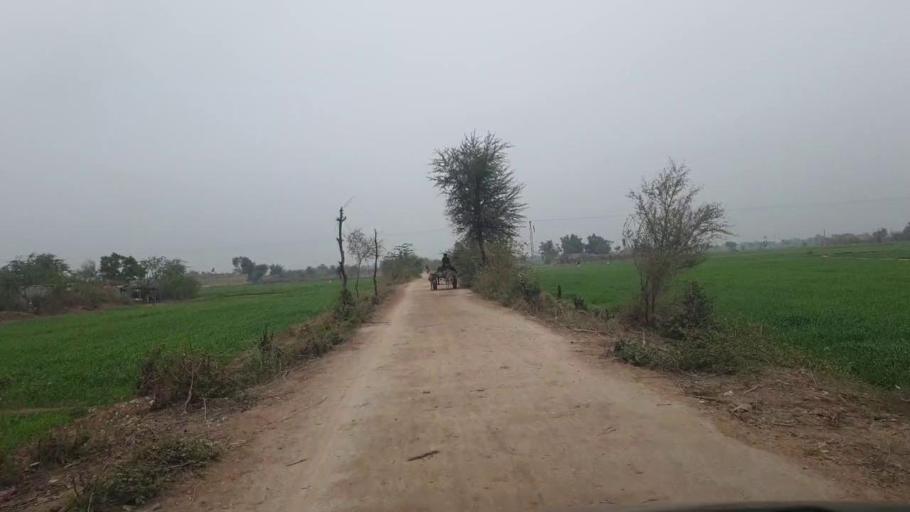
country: PK
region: Sindh
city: Tando Adam
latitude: 25.8446
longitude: 68.7068
